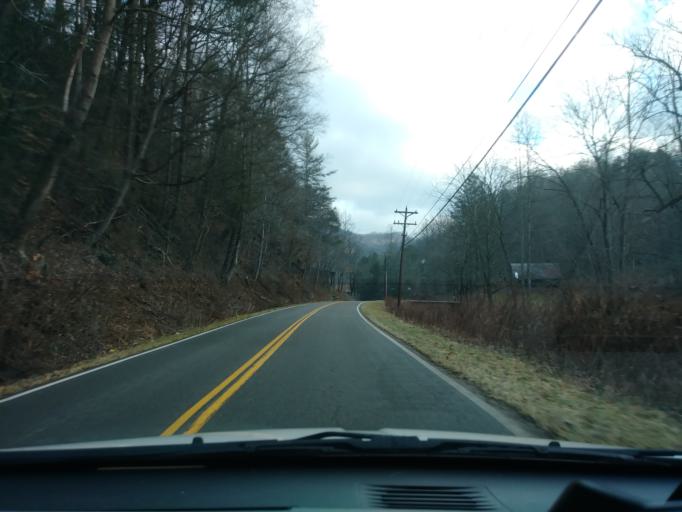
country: US
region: Tennessee
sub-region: Carter County
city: Elizabethton
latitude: 36.2224
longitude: -82.1956
